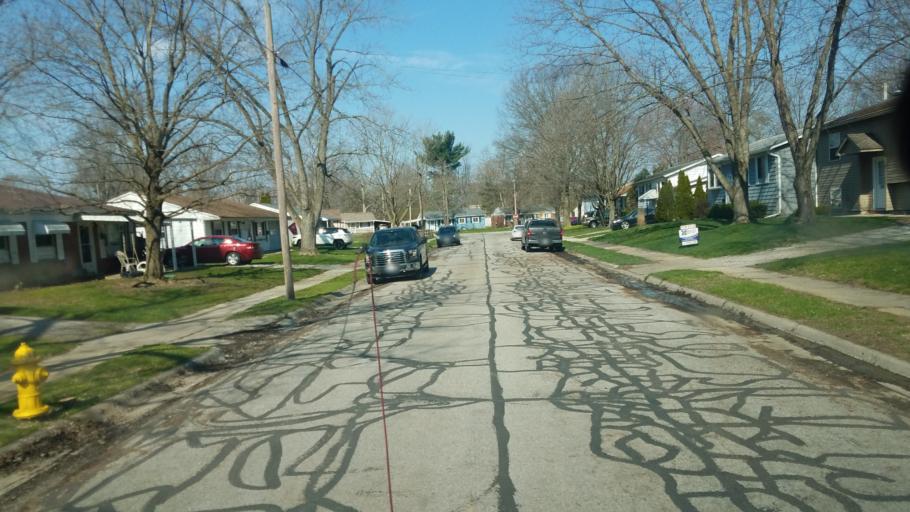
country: US
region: Ohio
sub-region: Delaware County
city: Delaware
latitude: 40.3013
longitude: -83.0509
